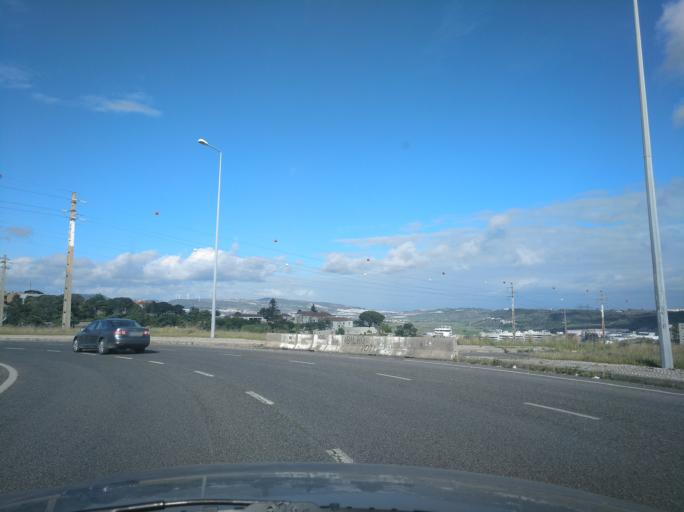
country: PT
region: Lisbon
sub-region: Loures
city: Loures
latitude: 38.8165
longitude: -9.1737
